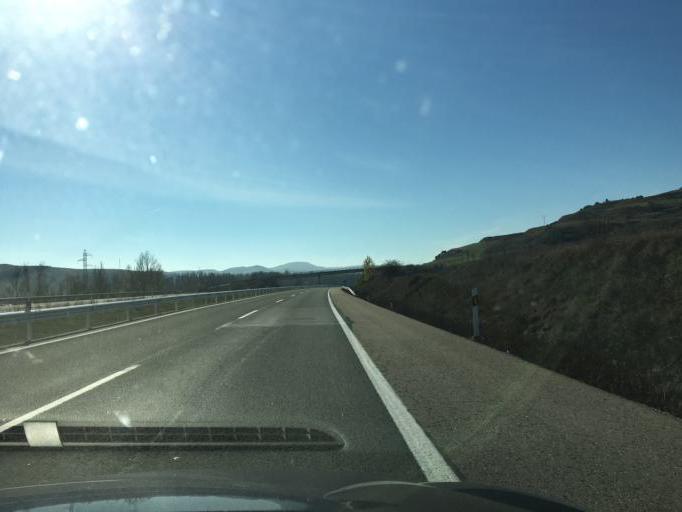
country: ES
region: Castille and Leon
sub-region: Provincia de Burgos
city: Pradanos de Bureba
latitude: 42.5054
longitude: -3.3500
